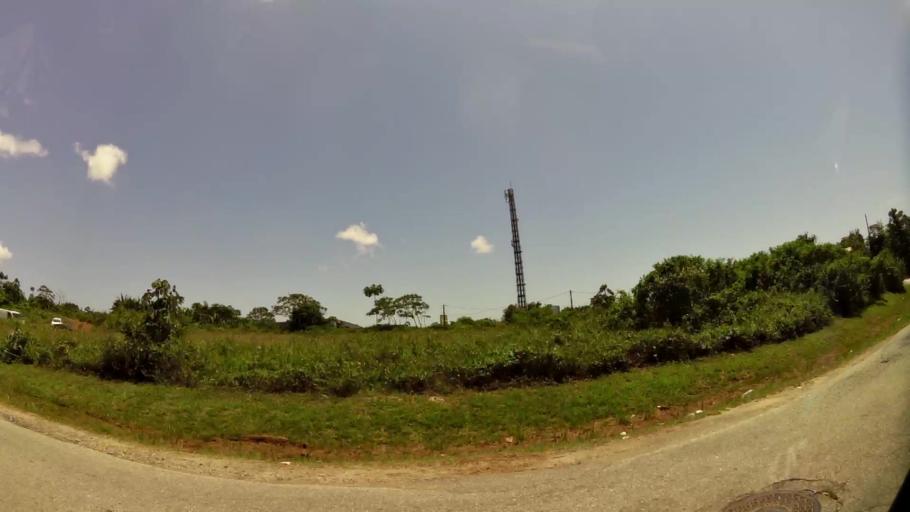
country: GF
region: Guyane
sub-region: Guyane
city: Cayenne
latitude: 4.8960
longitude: -52.3337
